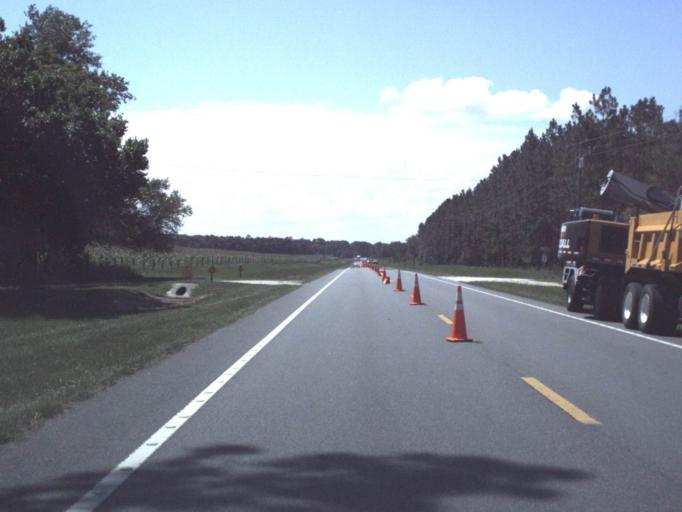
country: US
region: Florida
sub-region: Lafayette County
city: Mayo
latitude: 30.0796
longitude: -83.2146
